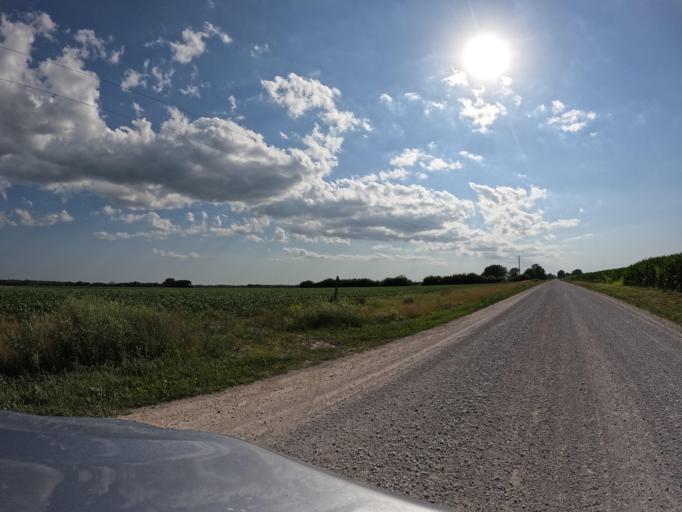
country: US
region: Iowa
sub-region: Appanoose County
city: Centerville
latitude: 40.7179
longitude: -93.0091
